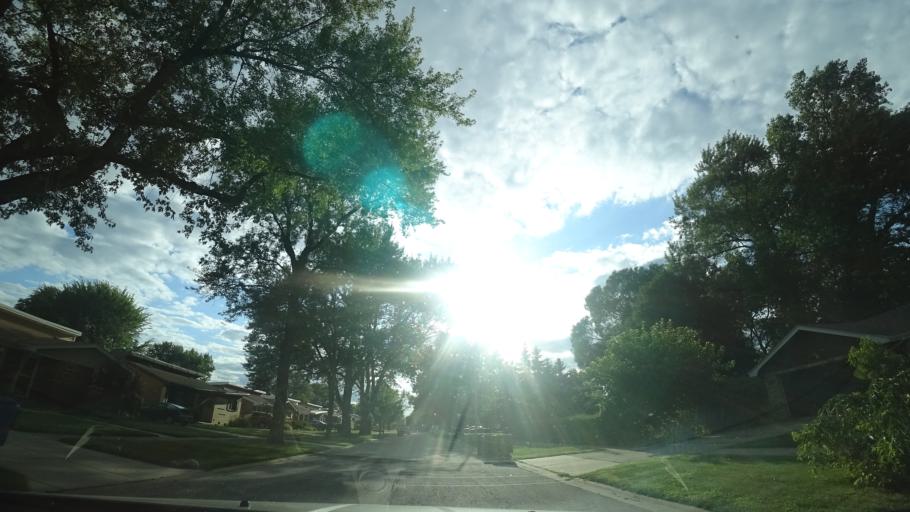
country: US
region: Illinois
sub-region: Cook County
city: Merrionette Park
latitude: 41.7004
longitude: -87.7211
